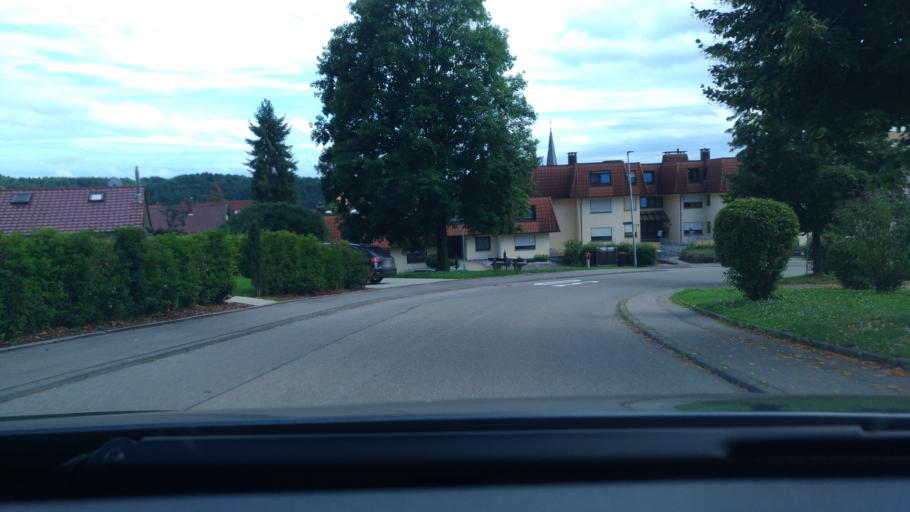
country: DE
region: Baden-Wuerttemberg
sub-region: Freiburg Region
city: Stockach
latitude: 47.8561
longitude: 9.0137
